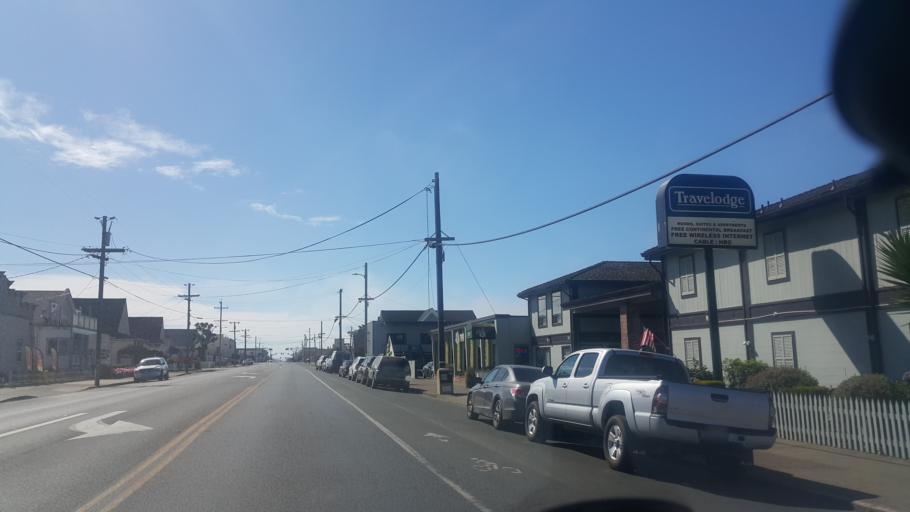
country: US
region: California
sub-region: Mendocino County
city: Fort Bragg
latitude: 39.4505
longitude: -123.8059
